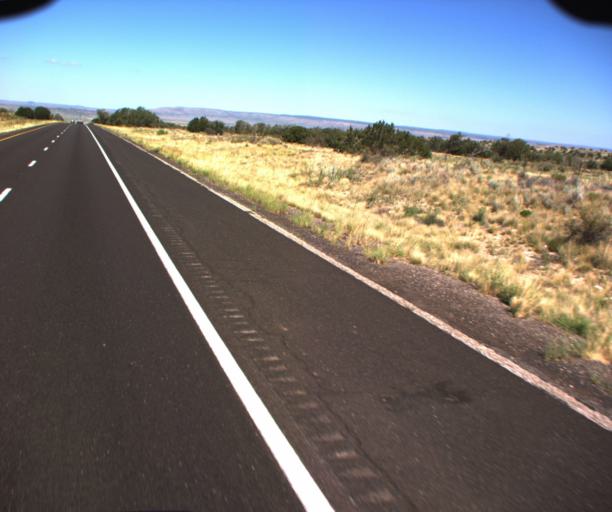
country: US
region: Arizona
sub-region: Yavapai County
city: Paulden
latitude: 35.2782
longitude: -112.7765
